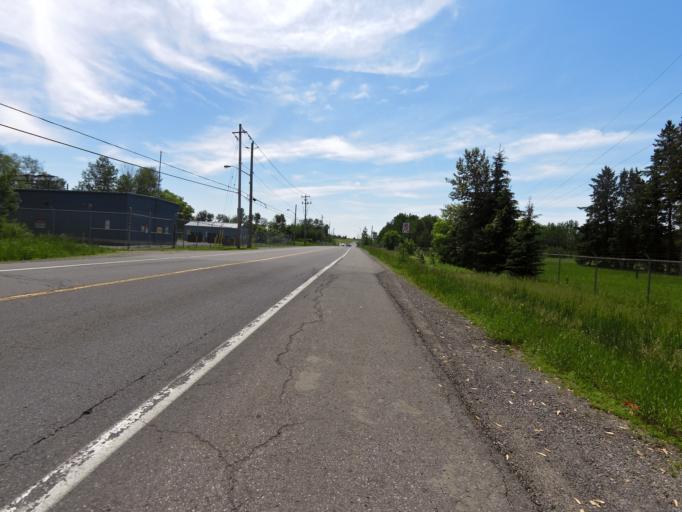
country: CA
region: Ontario
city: Ottawa
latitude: 45.3343
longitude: -75.6597
